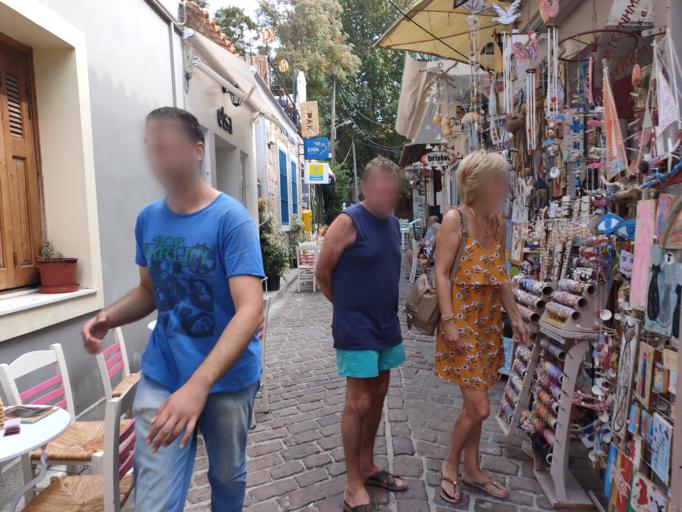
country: GR
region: North Aegean
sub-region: Nomos Lesvou
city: Petra
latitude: 39.3277
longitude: 26.1755
